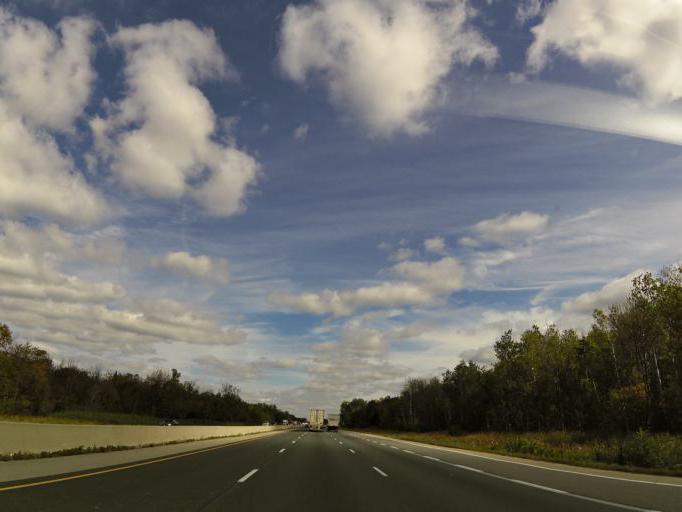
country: CA
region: Ontario
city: Dorchester
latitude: 42.9665
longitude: -81.0096
